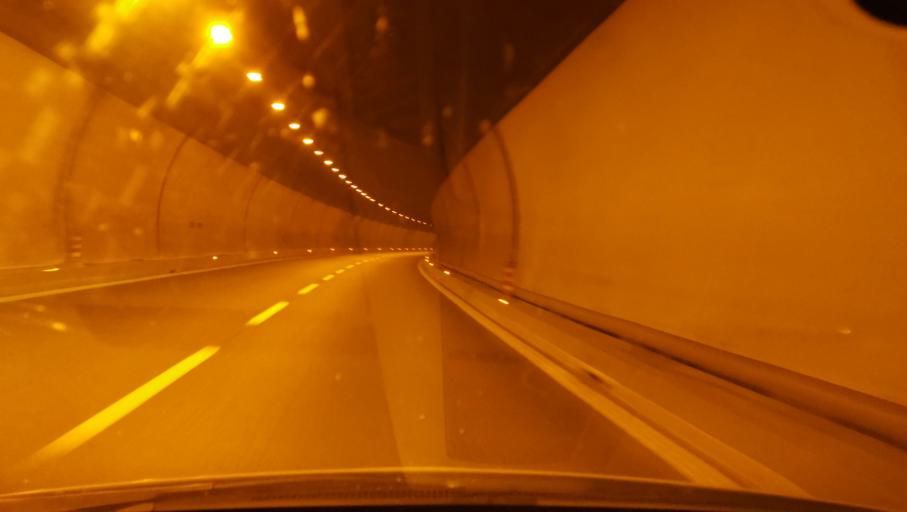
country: IT
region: Piedmont
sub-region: Provincia di Torino
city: Caselette
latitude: 45.0808
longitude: 7.4972
